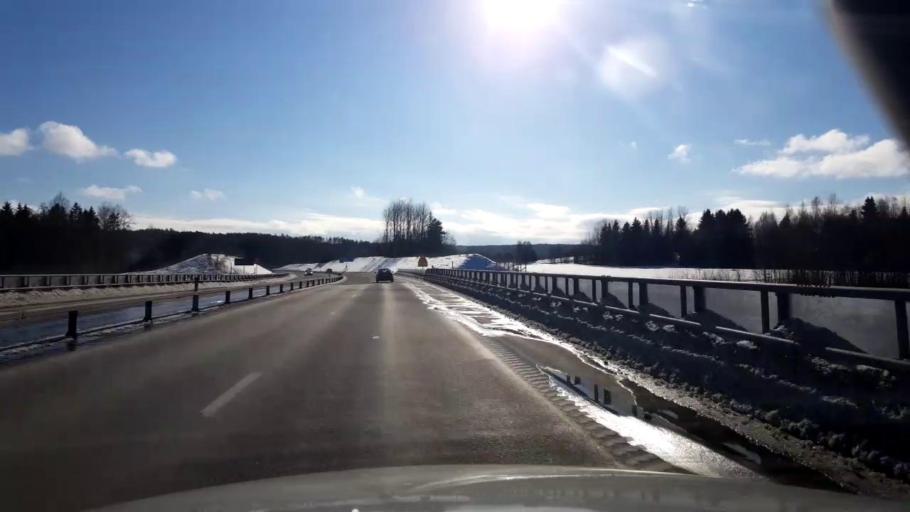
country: SE
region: Vaesternorrland
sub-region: Sundsvalls Kommun
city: Nolby
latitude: 62.2723
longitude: 17.3451
